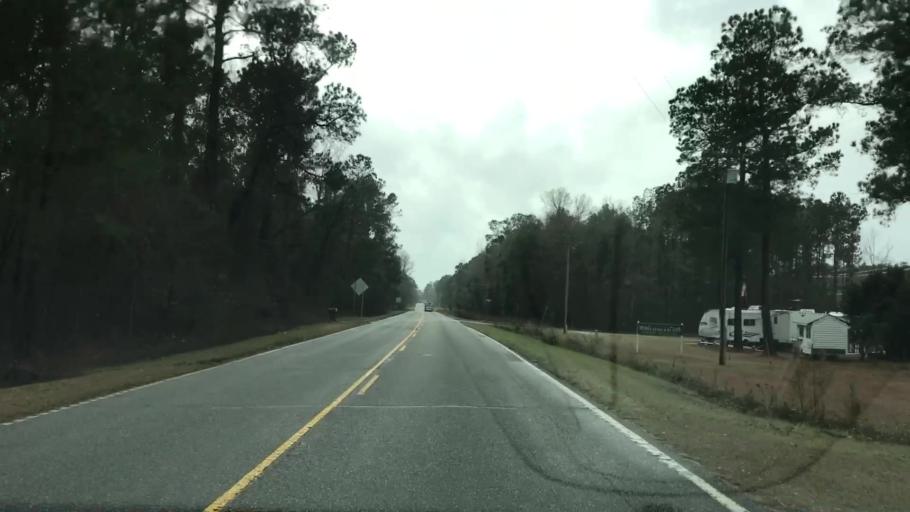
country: US
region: South Carolina
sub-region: Georgetown County
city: Murrells Inlet
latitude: 33.6491
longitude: -79.1701
